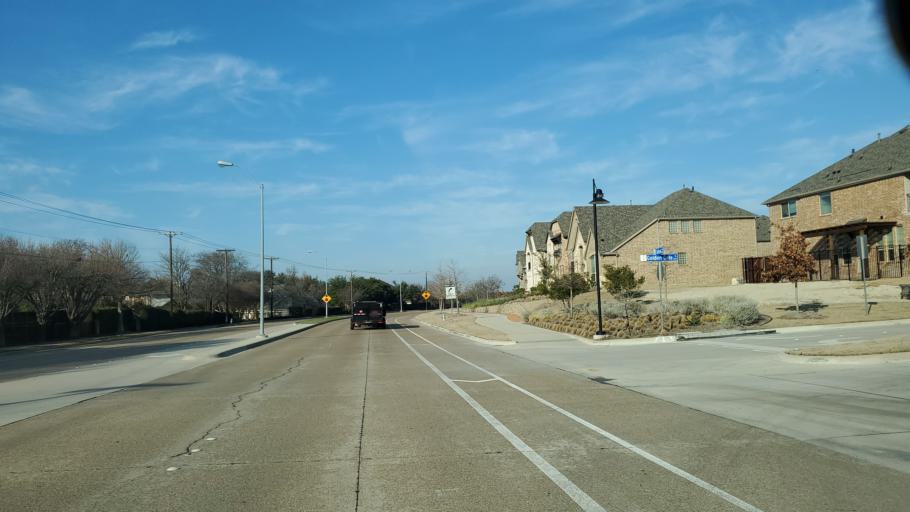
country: US
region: Texas
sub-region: Collin County
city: Plano
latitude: 32.9864
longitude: -96.7168
